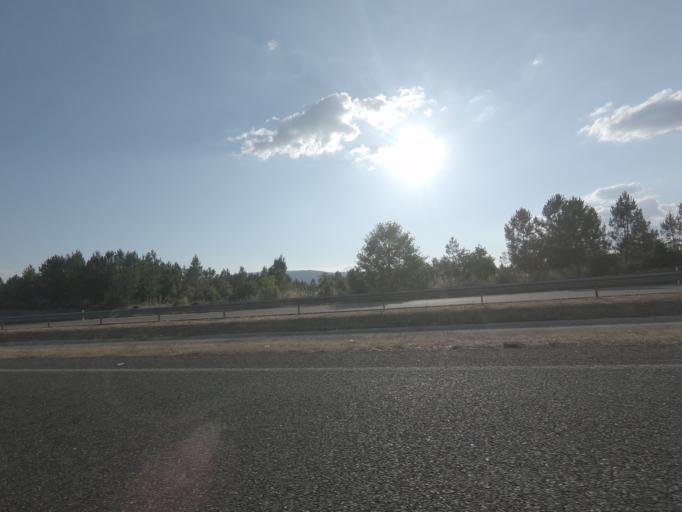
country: ES
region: Galicia
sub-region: Provincia de Ourense
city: Oimbra
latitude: 41.8789
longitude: -7.4292
